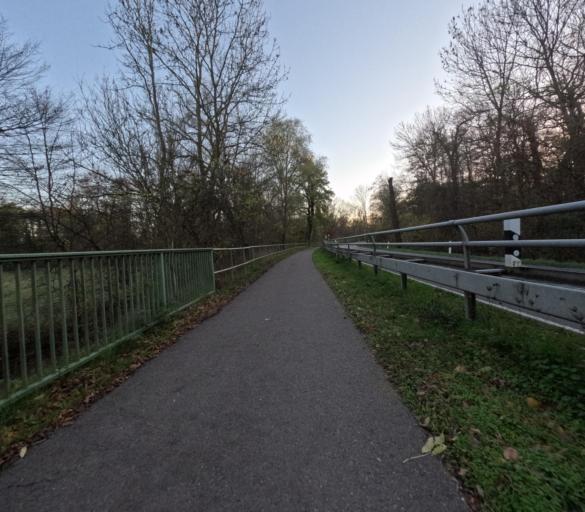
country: DE
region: Saxony
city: Schkeuditz
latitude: 51.3825
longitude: 12.2238
